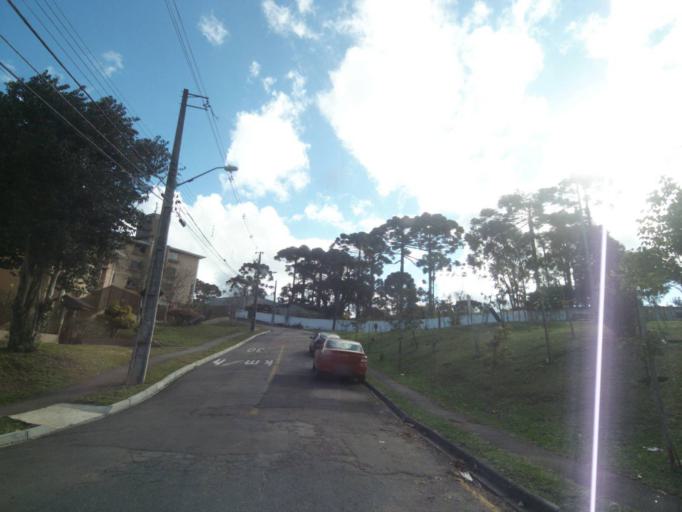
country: BR
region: Parana
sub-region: Sao Jose Dos Pinhais
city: Sao Jose dos Pinhais
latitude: -25.5303
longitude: -49.2831
